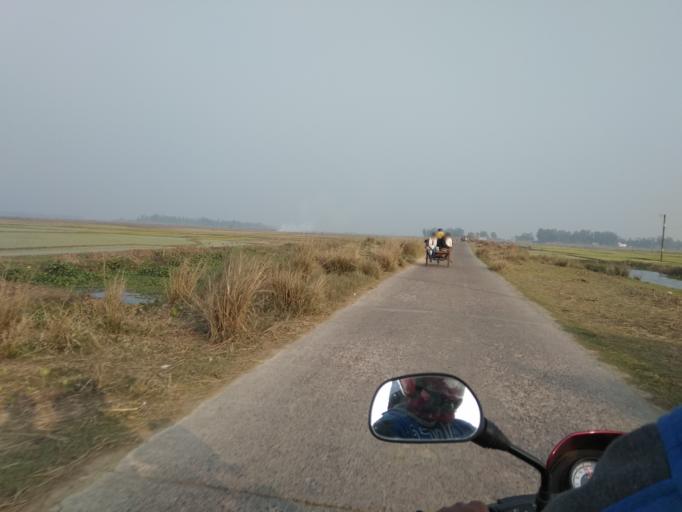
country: BD
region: Rajshahi
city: Ishurdi
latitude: 24.4953
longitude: 89.1909
